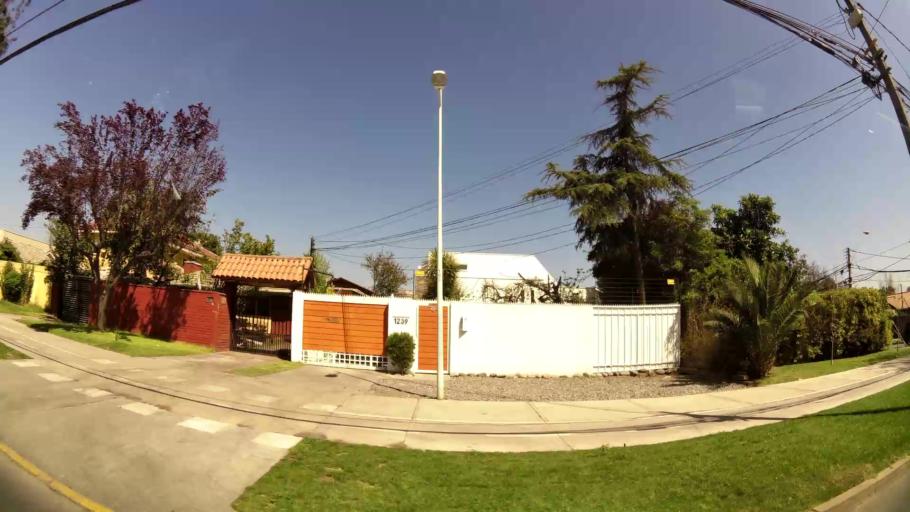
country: CL
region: Santiago Metropolitan
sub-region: Provincia de Santiago
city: Villa Presidente Frei, Nunoa, Santiago, Chile
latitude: -33.4221
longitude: -70.5488
